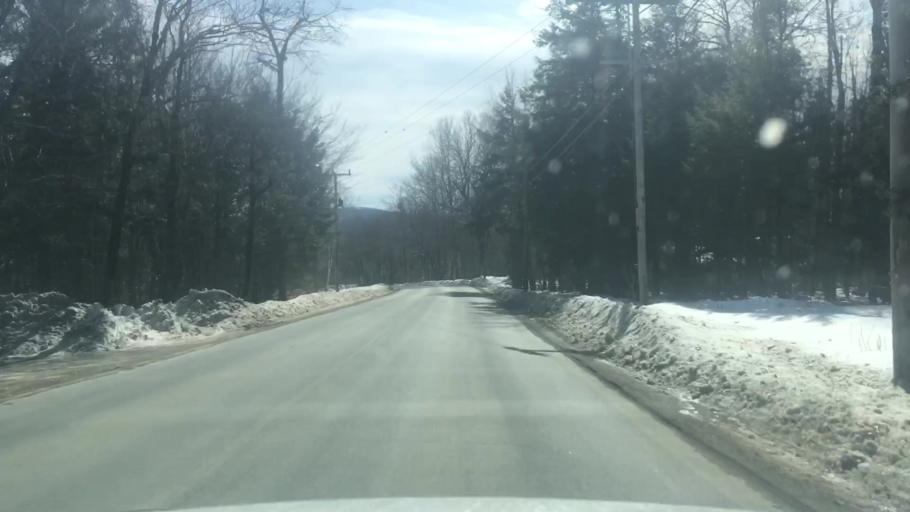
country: US
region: Maine
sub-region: Penobscot County
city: Holden
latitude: 44.7606
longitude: -68.6416
